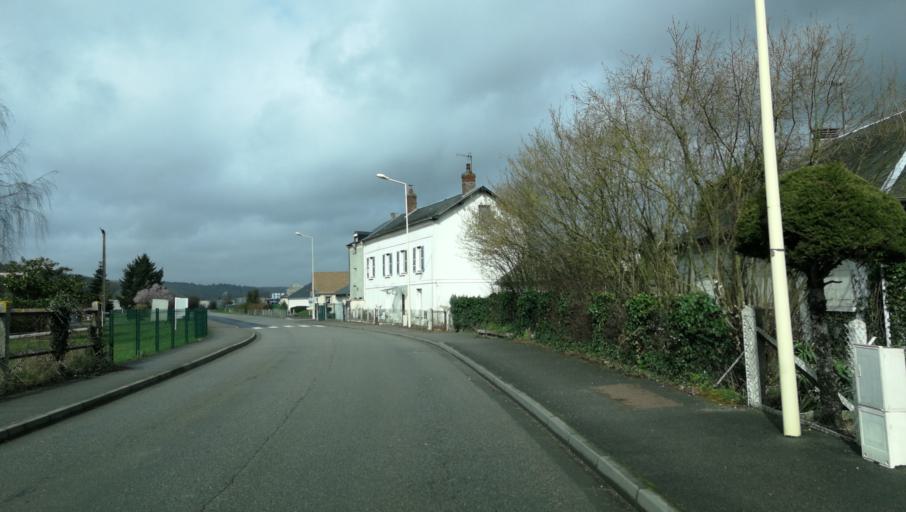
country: FR
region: Haute-Normandie
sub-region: Departement de l'Eure
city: Brionne
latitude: 49.2006
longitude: 0.7156
